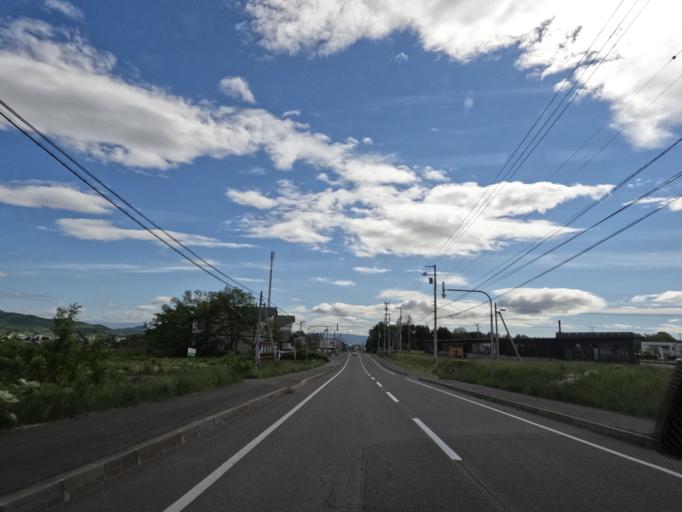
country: JP
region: Hokkaido
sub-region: Asahikawa-shi
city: Asahikawa
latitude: 43.8302
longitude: 142.5290
